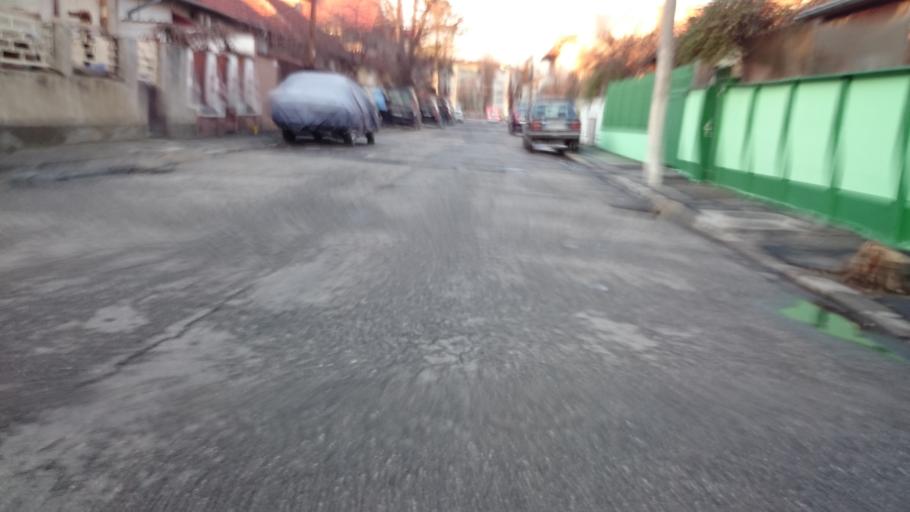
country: RO
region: Bucuresti
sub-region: Municipiul Bucuresti
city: Bucuresti
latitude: 44.4251
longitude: 26.0587
